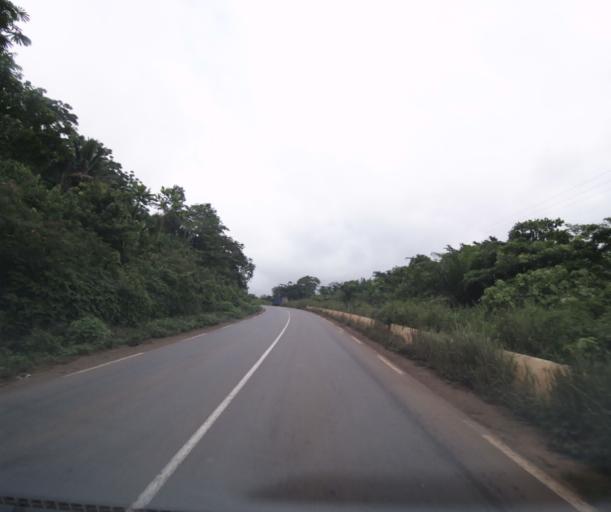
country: CM
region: Centre
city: Mbankomo
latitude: 3.7973
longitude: 11.3651
